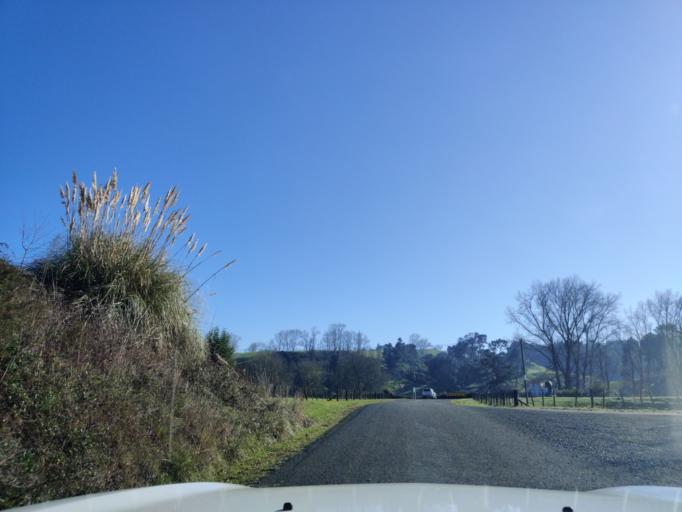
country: NZ
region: Waikato
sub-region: Matamata-Piako District
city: Matamata
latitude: -37.9865
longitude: 175.7142
